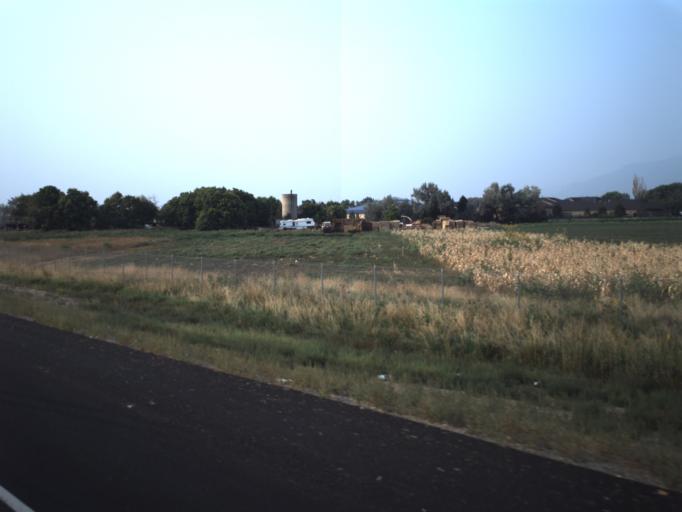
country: US
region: Utah
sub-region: Davis County
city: Kaysville
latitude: 41.0428
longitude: -111.9540
